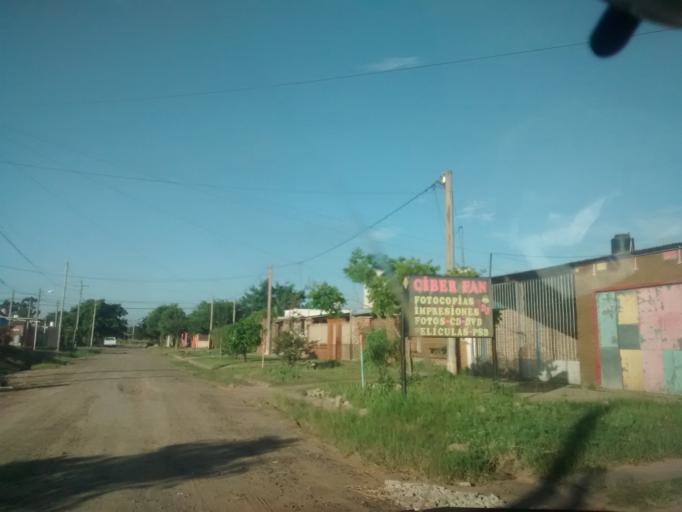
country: AR
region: Chaco
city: Fontana
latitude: -27.4581
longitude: -59.0324
